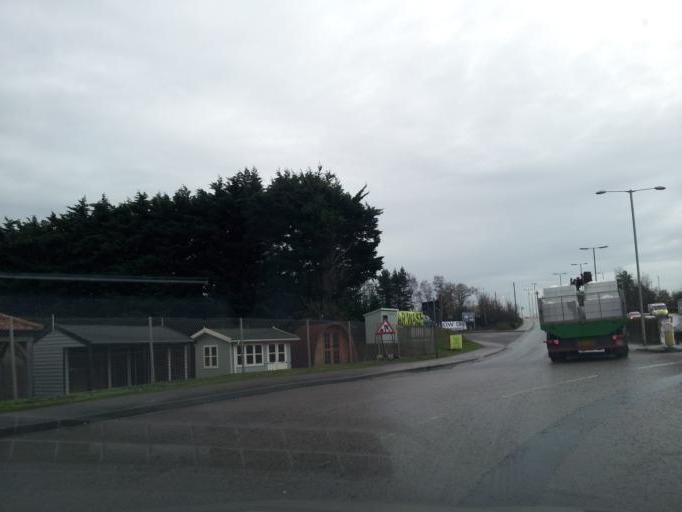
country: GB
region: England
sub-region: Norfolk
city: Costessey
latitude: 52.6536
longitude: 1.1860
